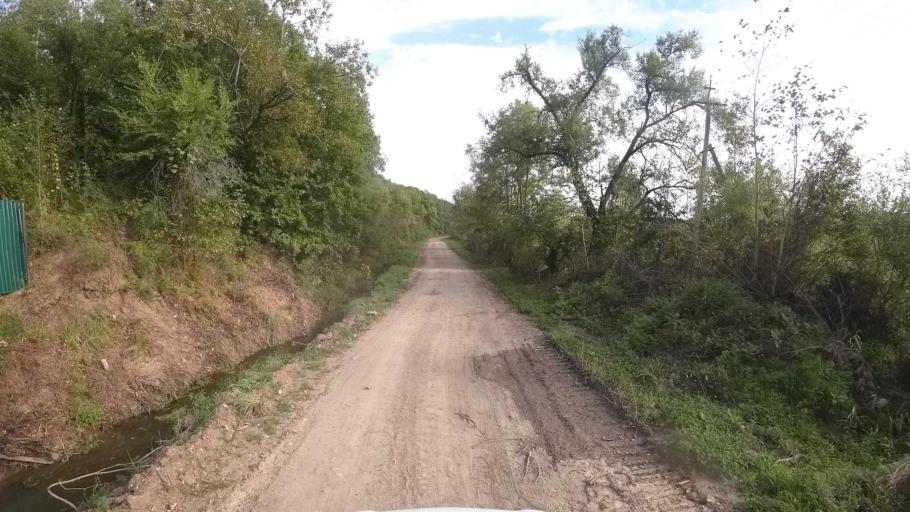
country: RU
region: Primorskiy
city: Dostoyevka
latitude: 44.3066
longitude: 133.4667
